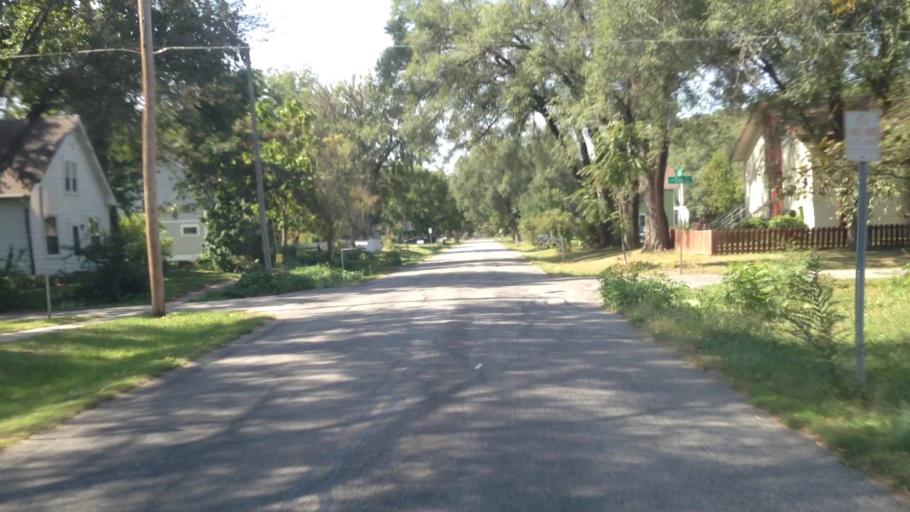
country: US
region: Kansas
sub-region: Douglas County
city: Lawrence
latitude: 38.9824
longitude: -95.2282
